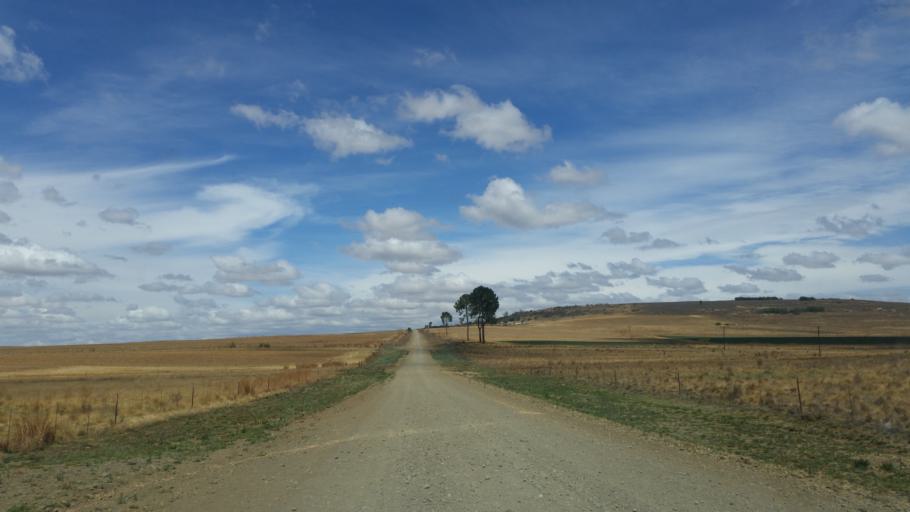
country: ZA
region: Orange Free State
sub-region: Thabo Mofutsanyana District Municipality
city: Bethlehem
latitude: -28.2403
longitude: 28.5769
